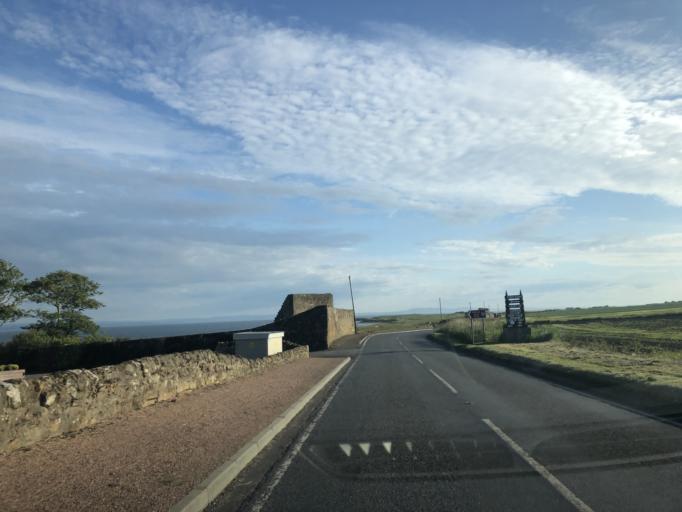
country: GB
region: Scotland
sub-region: Fife
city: Saint Monance
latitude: 56.1975
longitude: -2.7944
